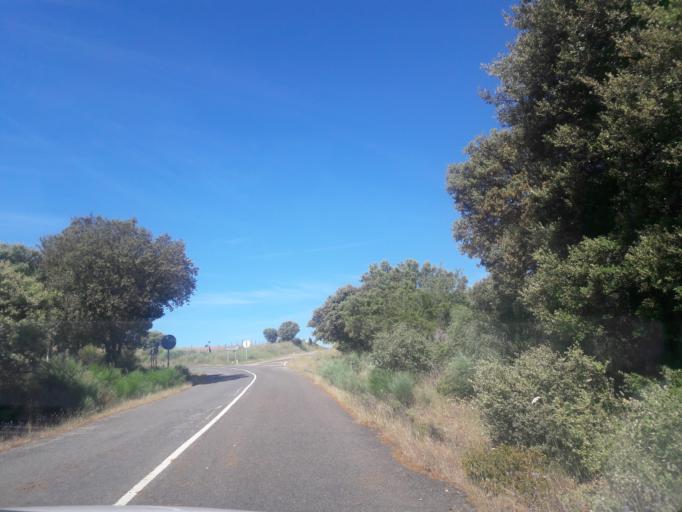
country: ES
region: Castille and Leon
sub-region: Provincia de Salamanca
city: Saucelle
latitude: 41.0007
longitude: -6.7376
